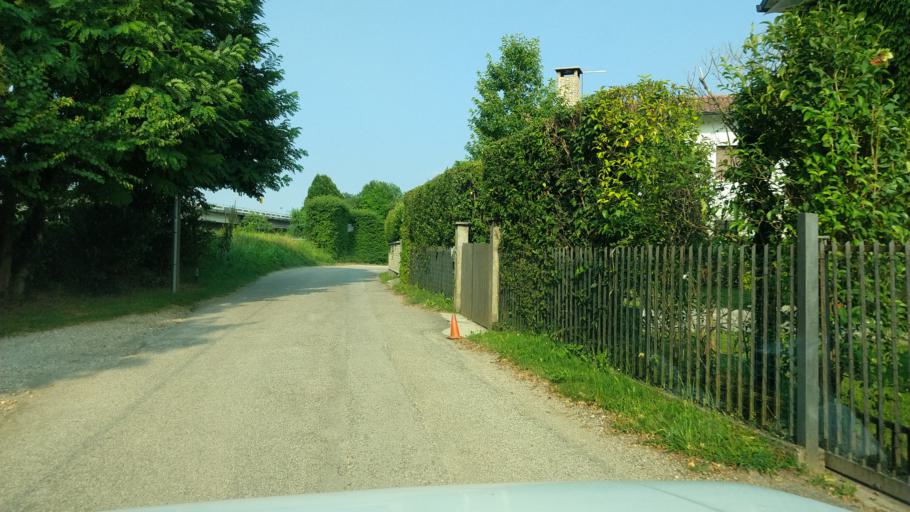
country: IT
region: Veneto
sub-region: Provincia di Vicenza
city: Nove
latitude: 45.7379
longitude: 11.6890
